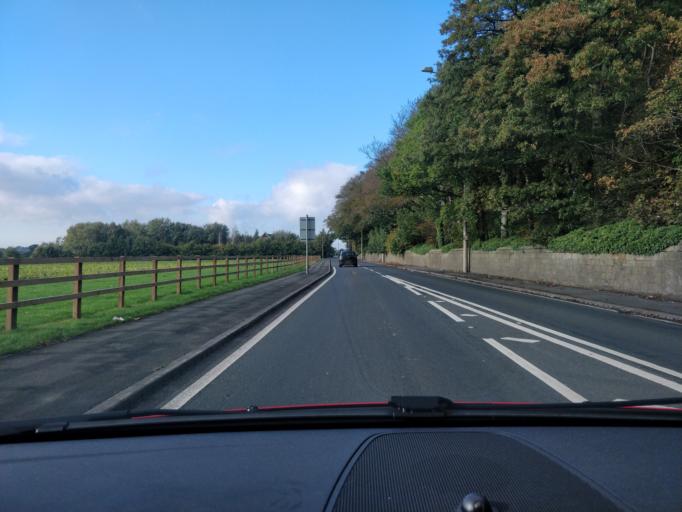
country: GB
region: England
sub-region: Lancashire
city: Ormskirk
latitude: 53.6016
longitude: -2.9282
